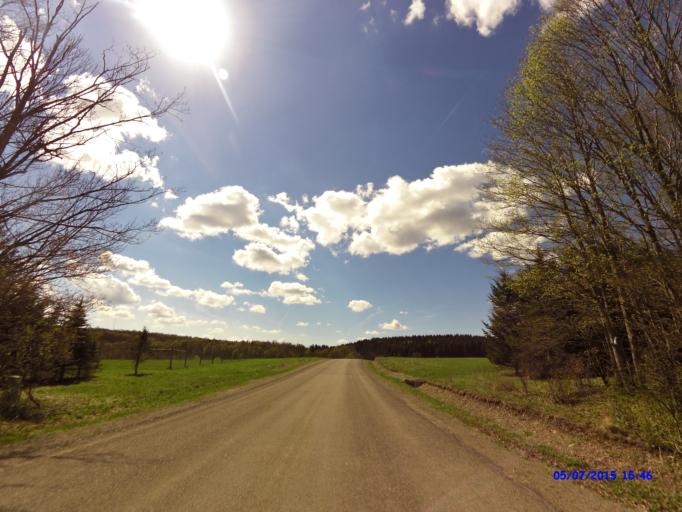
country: US
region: New York
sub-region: Cattaraugus County
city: Franklinville
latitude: 42.3153
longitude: -78.5573
